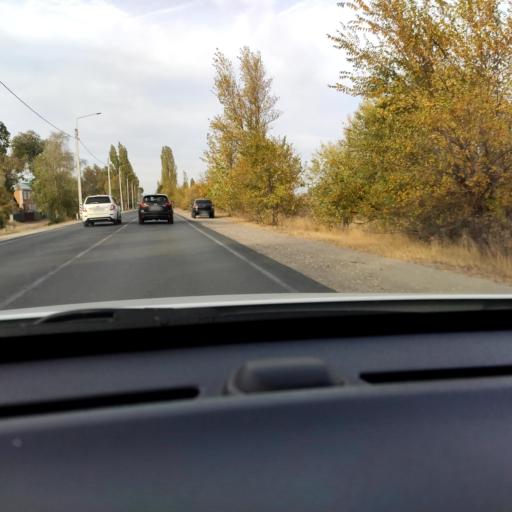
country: RU
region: Voronezj
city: Maslovka
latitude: 51.5681
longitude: 39.2460
